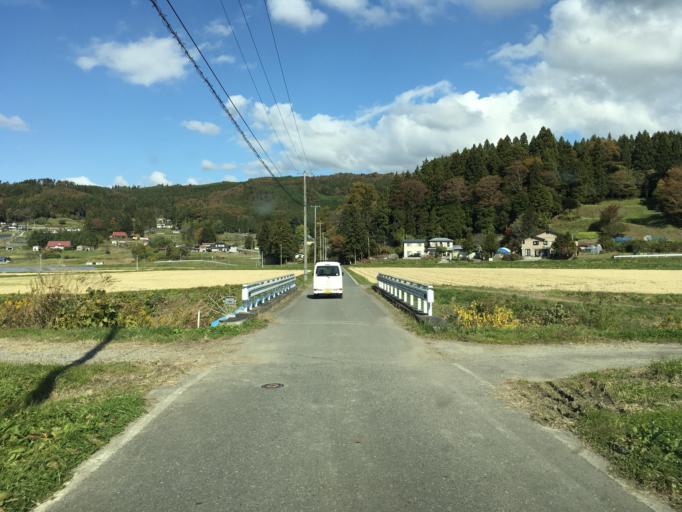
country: JP
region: Iwate
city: Ichinoseki
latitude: 38.9540
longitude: 141.3818
